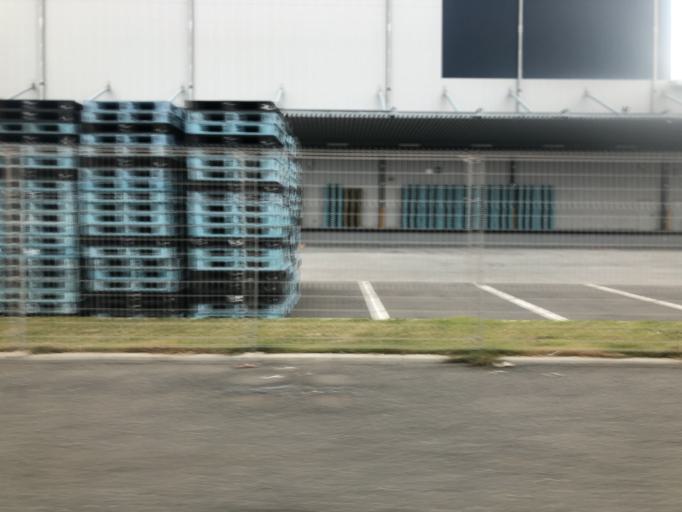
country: JP
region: Hyogo
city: Ashiya
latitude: 34.6850
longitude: 135.2542
